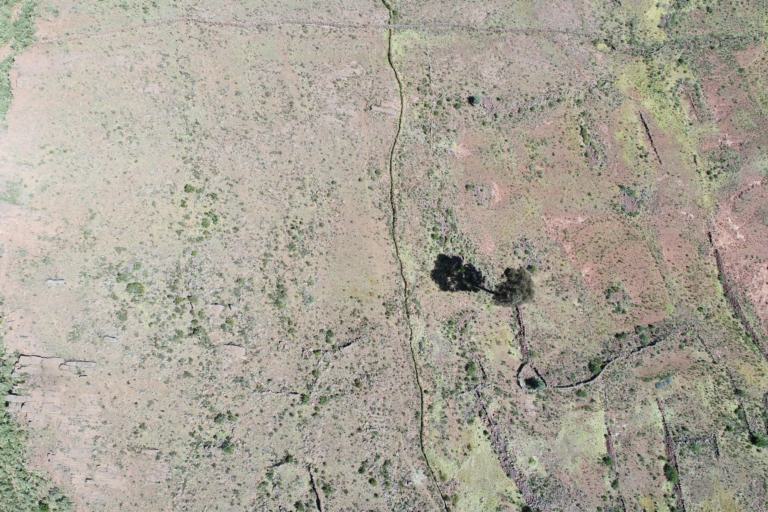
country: BO
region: La Paz
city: Tiahuanaco
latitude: -16.6089
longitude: -68.7706
